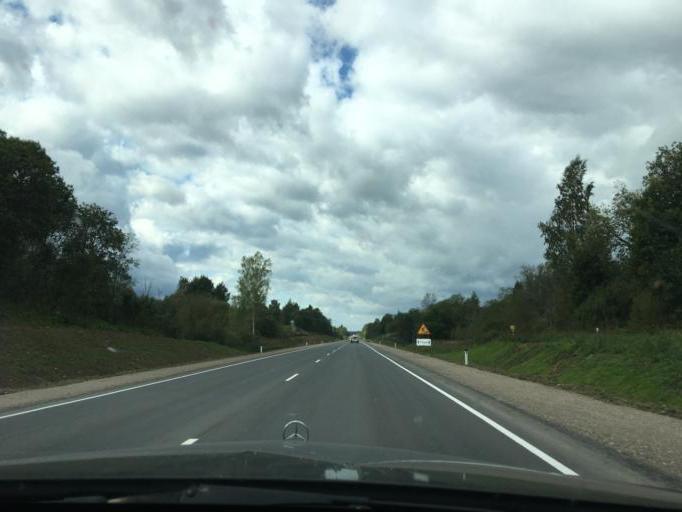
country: RU
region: Tverskaya
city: Toropets
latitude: 56.3066
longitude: 31.1132
